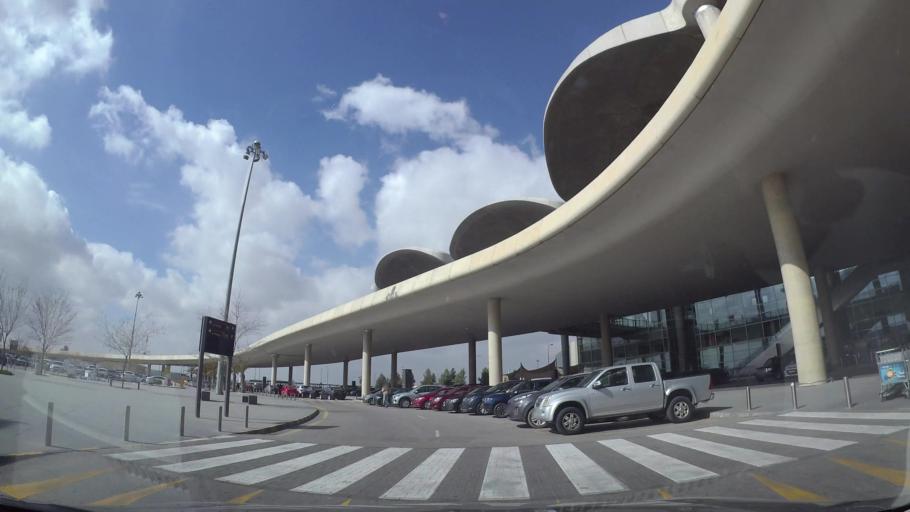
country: JO
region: Amman
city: Al Jizah
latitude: 31.7223
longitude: 35.9854
